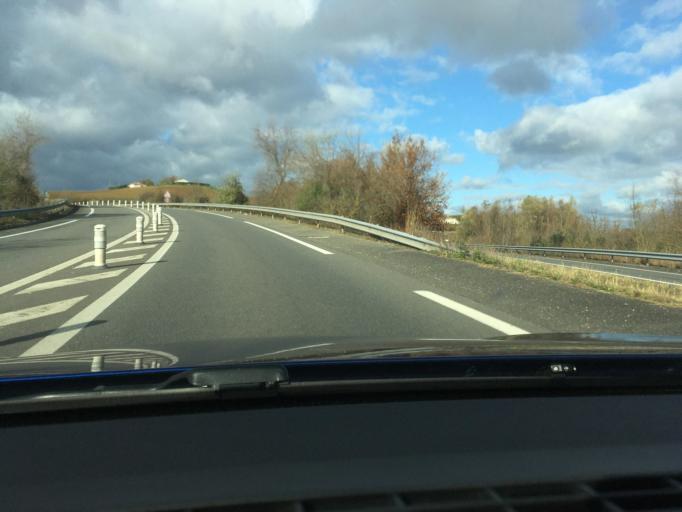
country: FR
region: Midi-Pyrenees
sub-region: Departement du Tarn-et-Garonne
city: Caussade
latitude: 44.1523
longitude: 1.5151
